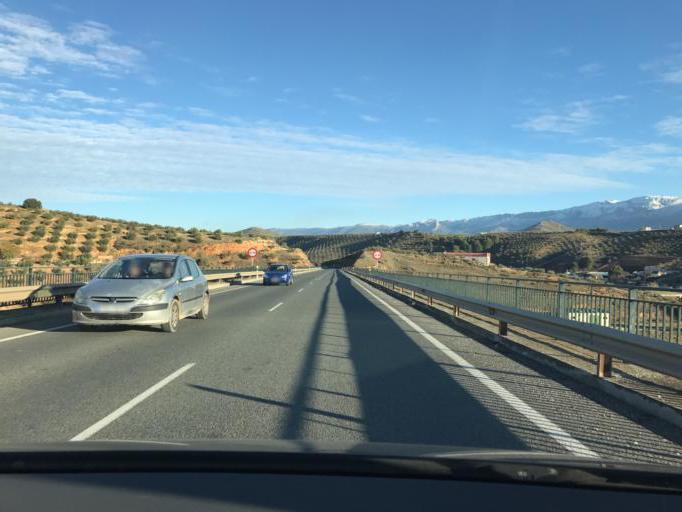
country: ES
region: Andalusia
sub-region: Provincia de Granada
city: Iznalloz
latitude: 37.4019
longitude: -3.5291
